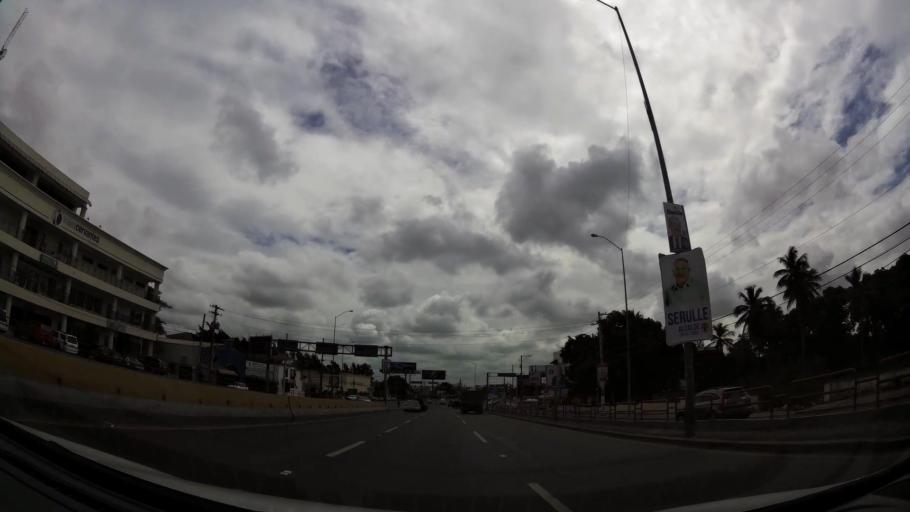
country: DO
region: Santiago
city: Santiago de los Caballeros
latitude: 19.4487
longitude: -70.6791
